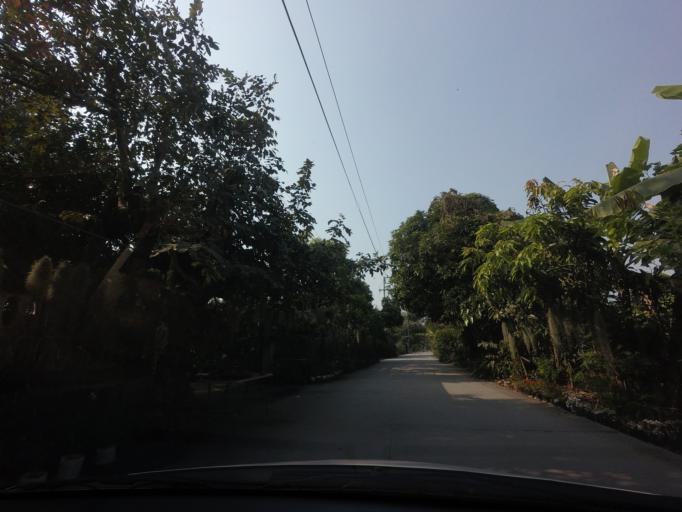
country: TH
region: Samut Sakhon
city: Krathum Baen
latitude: 13.6890
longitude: 100.2518
